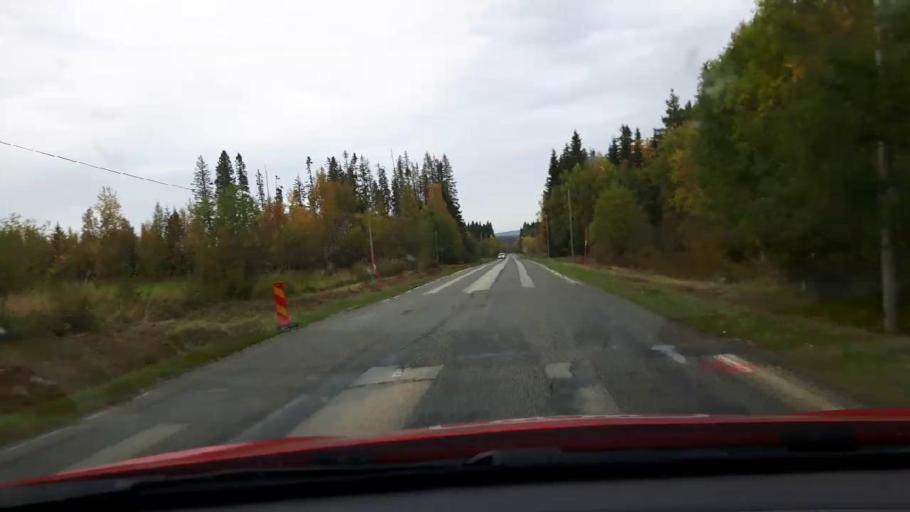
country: SE
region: Jaemtland
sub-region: Bergs Kommun
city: Hoverberg
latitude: 62.8593
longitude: 14.3786
